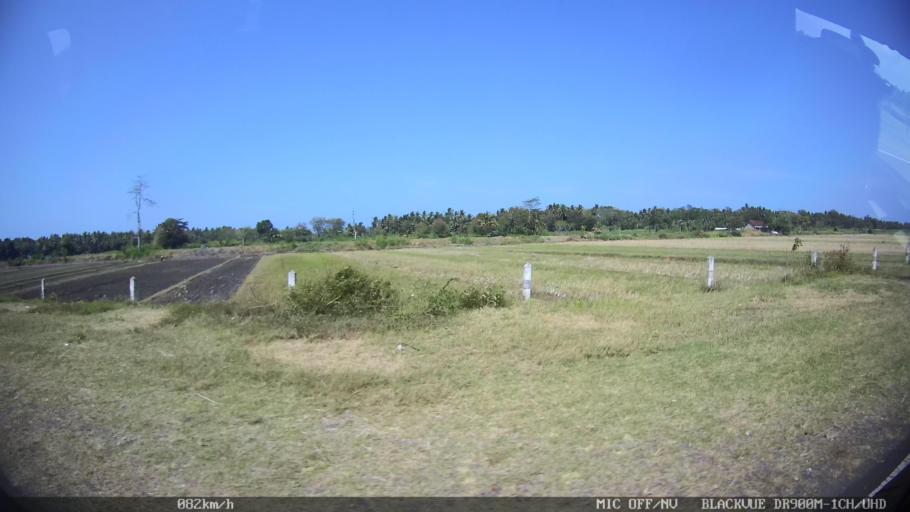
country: ID
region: Daerah Istimewa Yogyakarta
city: Srandakan
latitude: -7.9561
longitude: 110.1982
